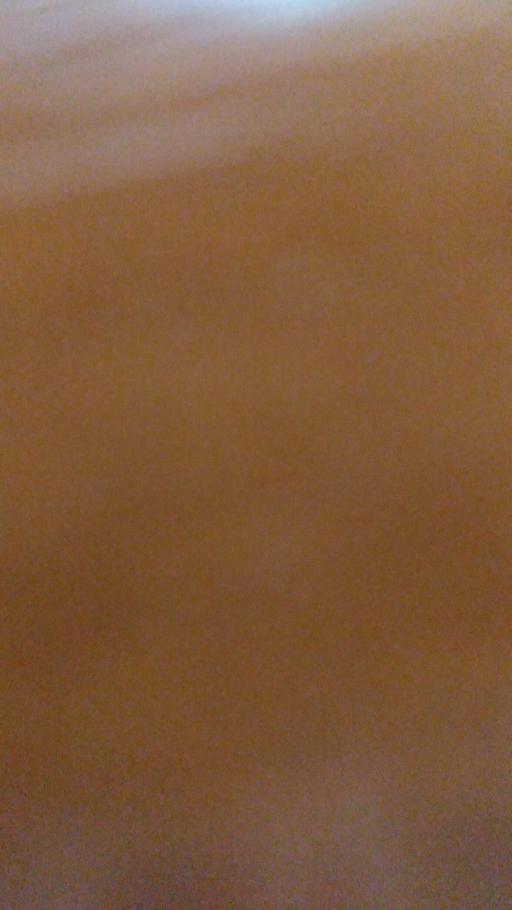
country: RU
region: Tula
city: Volovo
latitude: 53.5485
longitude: 38.1128
